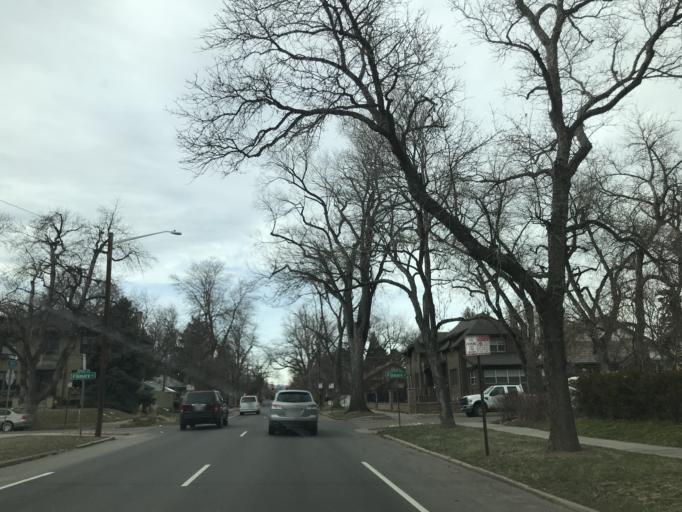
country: US
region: Colorado
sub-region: Arapahoe County
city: Glendale
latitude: 39.7292
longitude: -104.9525
